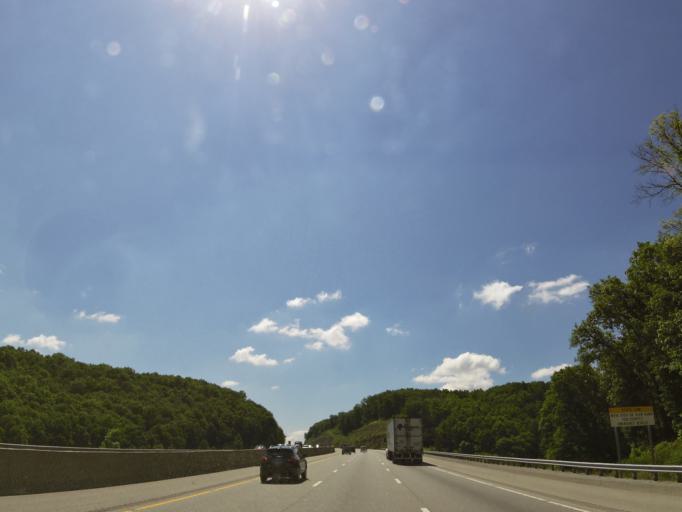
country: US
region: Kentucky
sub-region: Rockcastle County
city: Mount Vernon
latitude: 37.2336
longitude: -84.2282
